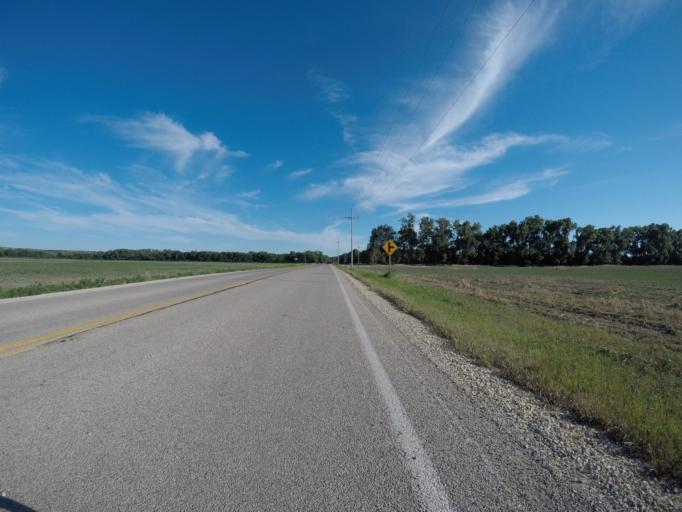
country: US
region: Kansas
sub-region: Riley County
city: Manhattan
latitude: 39.1475
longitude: -96.5814
